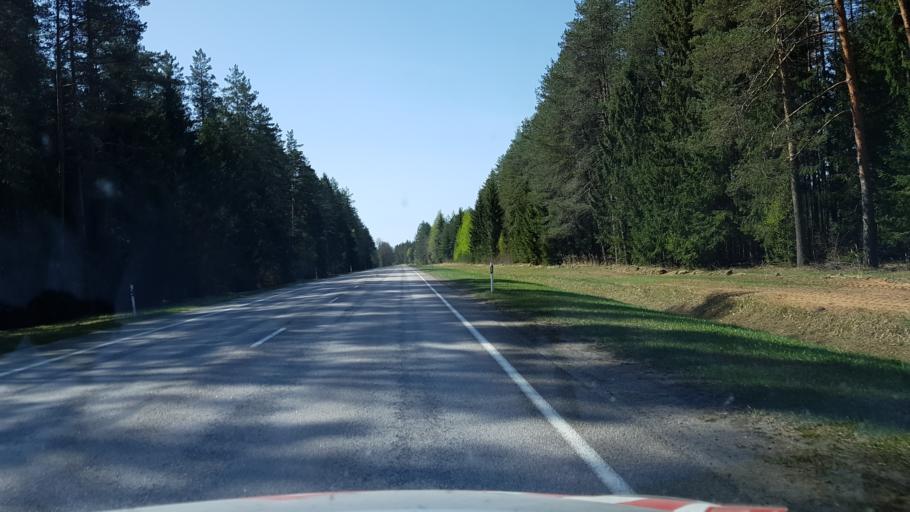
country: EE
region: Valgamaa
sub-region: Valga linn
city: Valga
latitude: 57.8217
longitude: 26.0497
